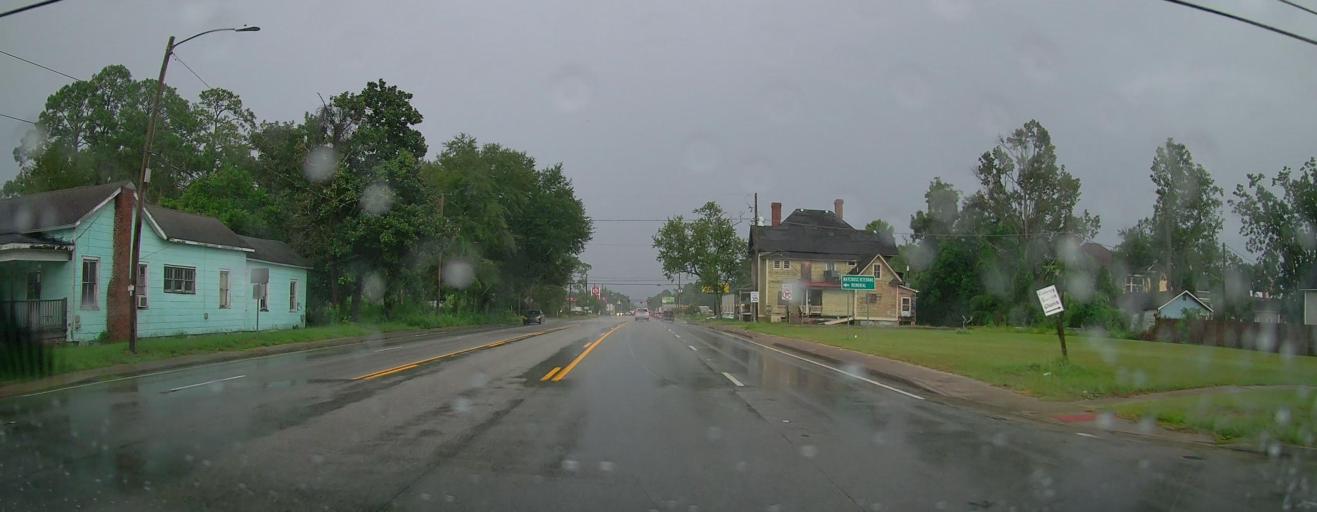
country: US
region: Georgia
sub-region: Ware County
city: Waycross
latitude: 31.2067
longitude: -82.3580
